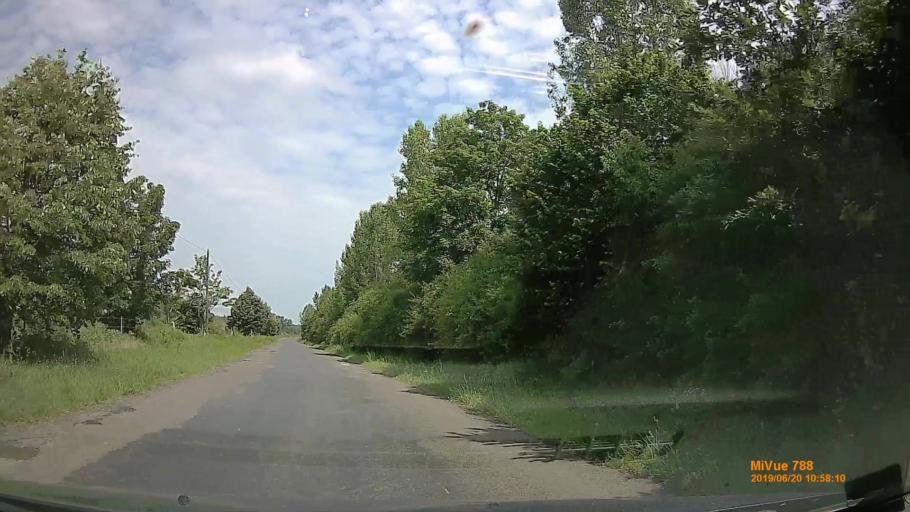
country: HU
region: Baranya
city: Mecseknadasd
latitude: 46.1575
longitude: 18.5176
